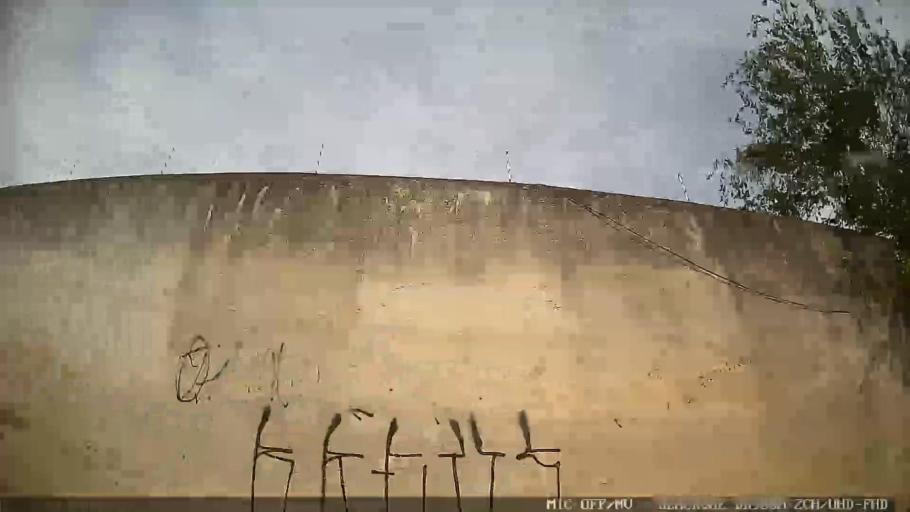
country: BR
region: Sao Paulo
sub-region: Braganca Paulista
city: Braganca Paulista
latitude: -22.9211
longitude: -46.5495
